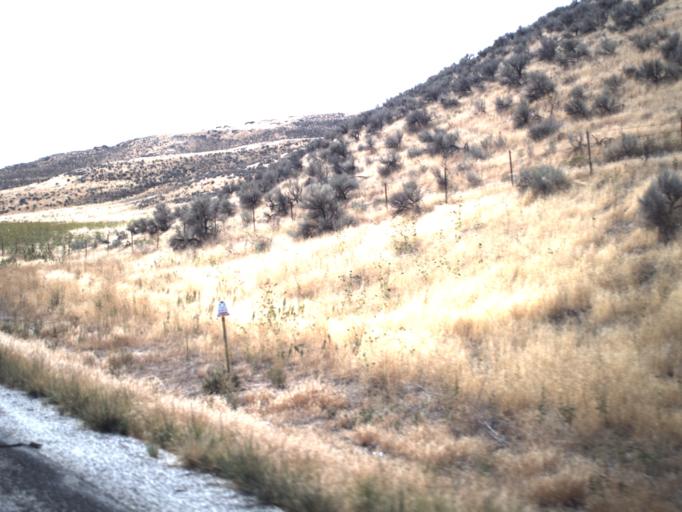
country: US
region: Utah
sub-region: Box Elder County
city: Tremonton
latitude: 41.6929
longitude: -112.4439
